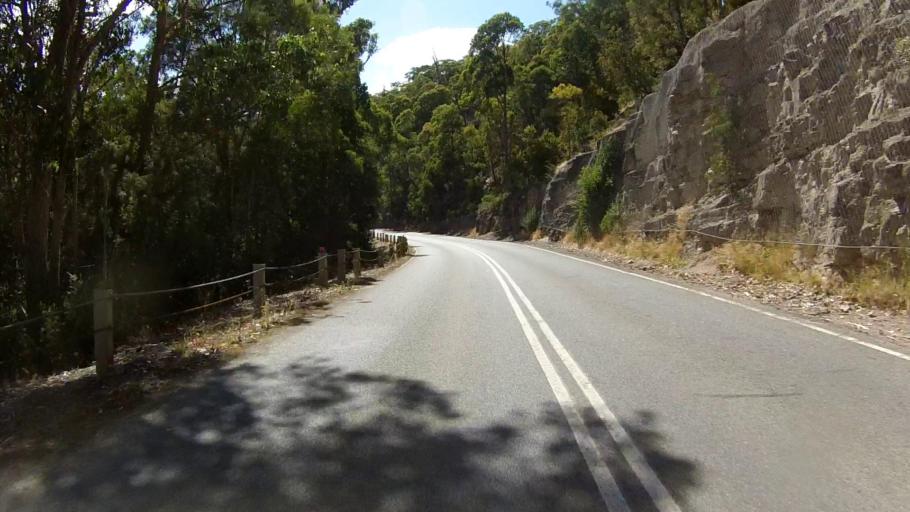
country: AU
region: Tasmania
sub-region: Derwent Valley
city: New Norfolk
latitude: -42.6856
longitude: 146.7263
